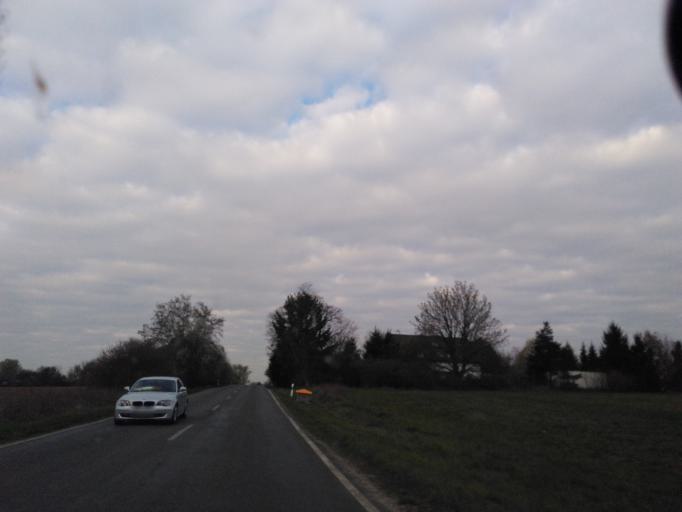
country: DE
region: Brandenburg
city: Protzel
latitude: 52.5689
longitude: 13.9813
